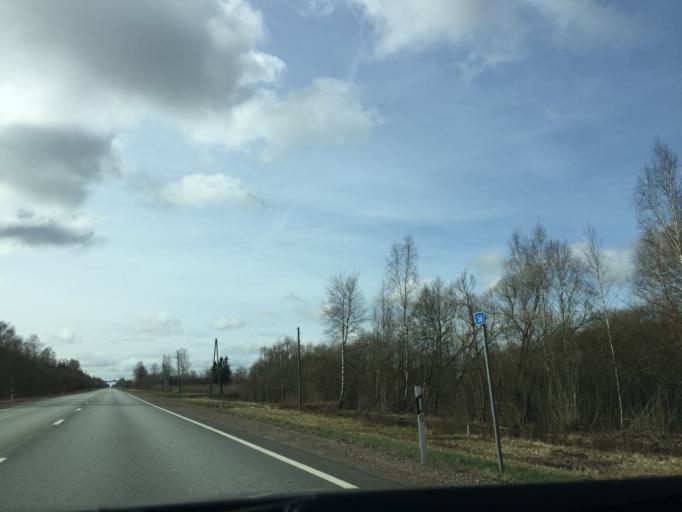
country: LV
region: Jelgava
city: Jelgava
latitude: 56.5450
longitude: 23.7086
